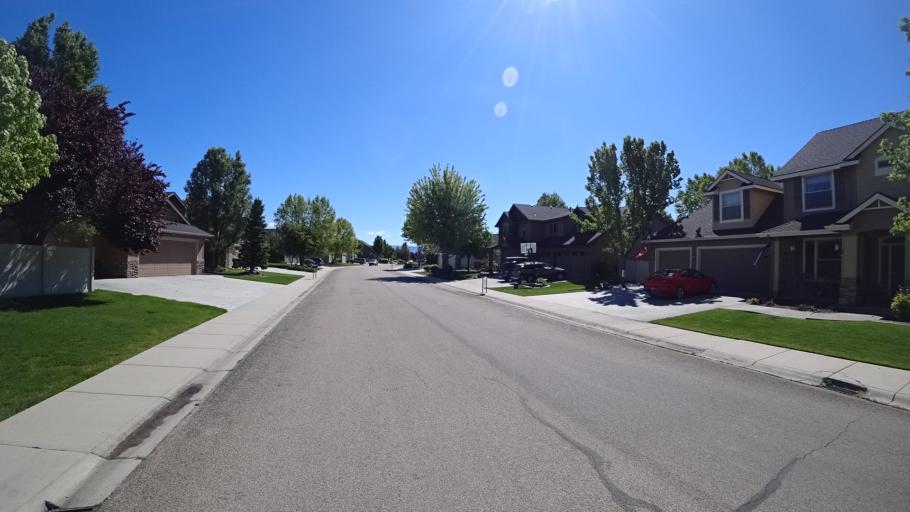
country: US
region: Idaho
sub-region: Ada County
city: Meridian
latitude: 43.6423
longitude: -116.3904
